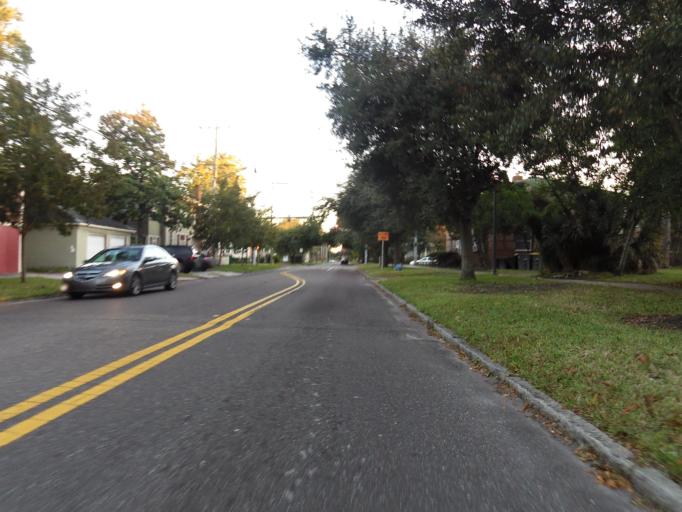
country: US
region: Florida
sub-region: Duval County
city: Jacksonville
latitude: 30.3147
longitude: -81.6893
